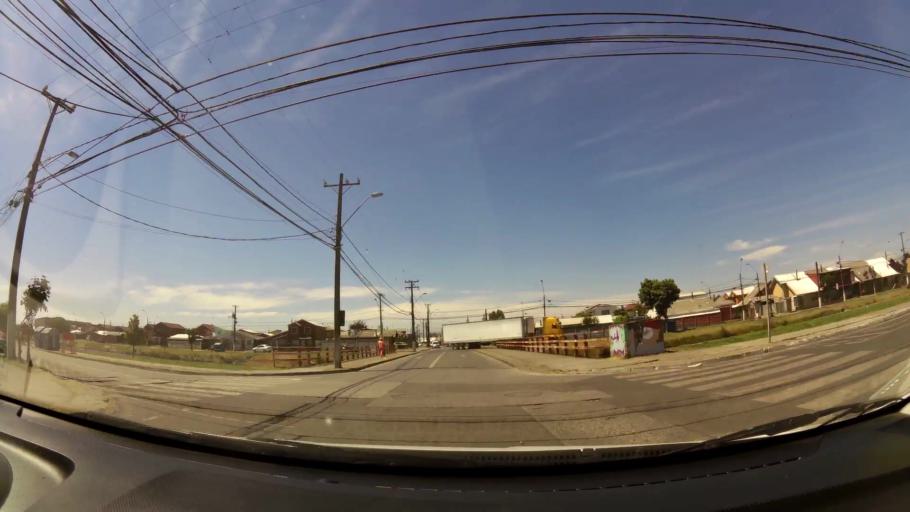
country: CL
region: Biobio
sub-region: Provincia de Concepcion
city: Talcahuano
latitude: -36.7546
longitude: -73.0852
